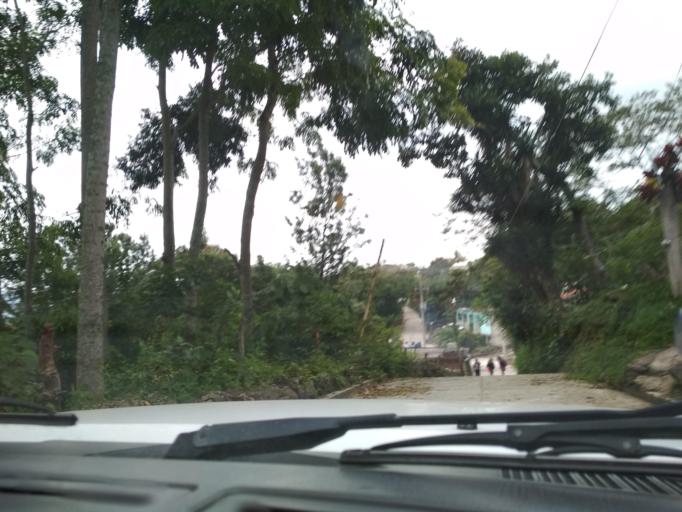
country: MX
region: Veracruz
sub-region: Naolinco
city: El Espinal
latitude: 19.5888
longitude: -96.8769
